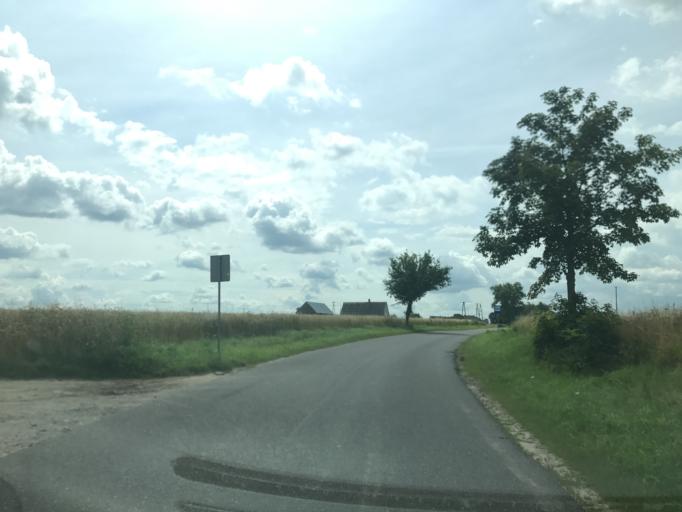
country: PL
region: Kujawsko-Pomorskie
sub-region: Powiat brodnicki
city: Bartniczka
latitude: 53.2377
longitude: 19.6004
